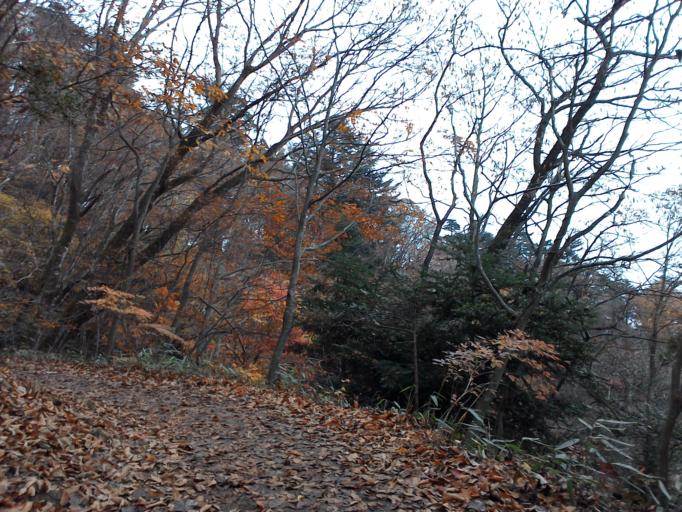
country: JP
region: Tokyo
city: Itsukaichi
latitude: 35.7773
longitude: 139.1437
